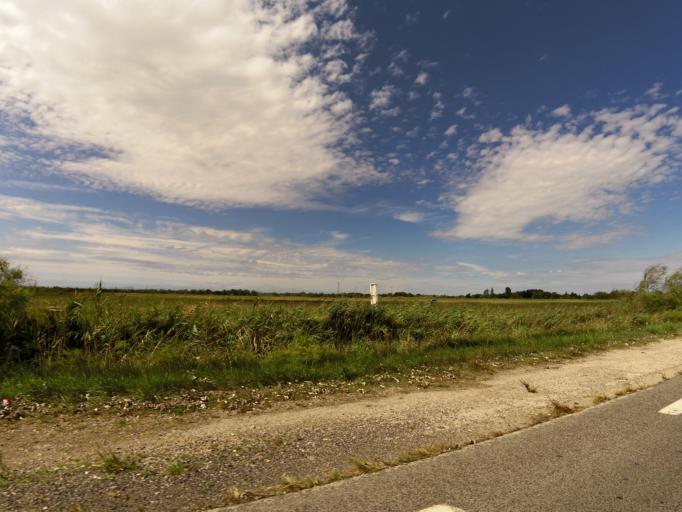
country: FR
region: Languedoc-Roussillon
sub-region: Departement du Gard
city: Le Grau-du-Roi
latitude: 43.5535
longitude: 4.1439
